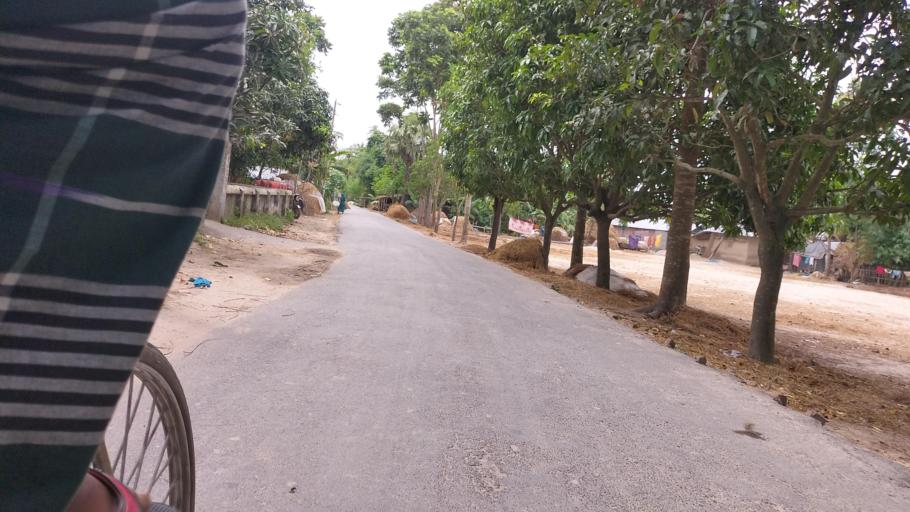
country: BD
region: Rajshahi
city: Rajshahi
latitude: 24.5176
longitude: 88.6236
